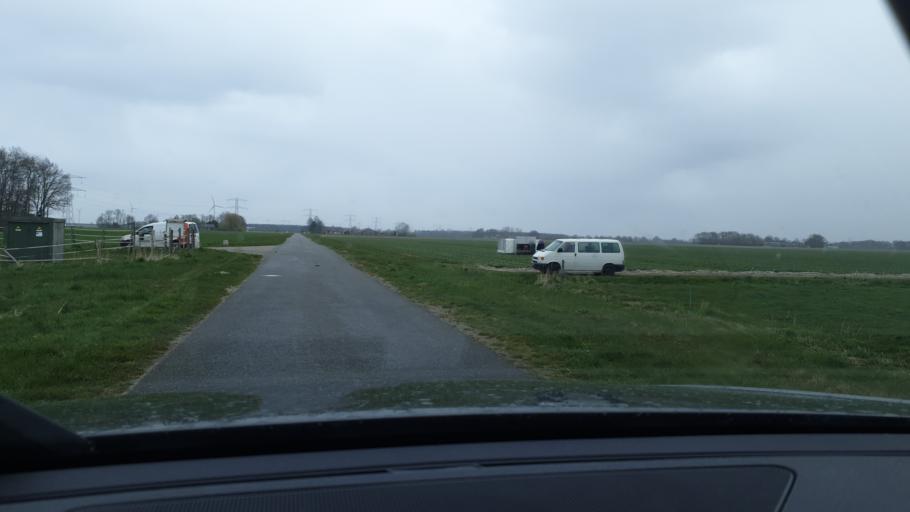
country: NL
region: Flevoland
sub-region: Gemeente Lelystad
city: Lelystad
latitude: 52.5723
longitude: 5.5494
